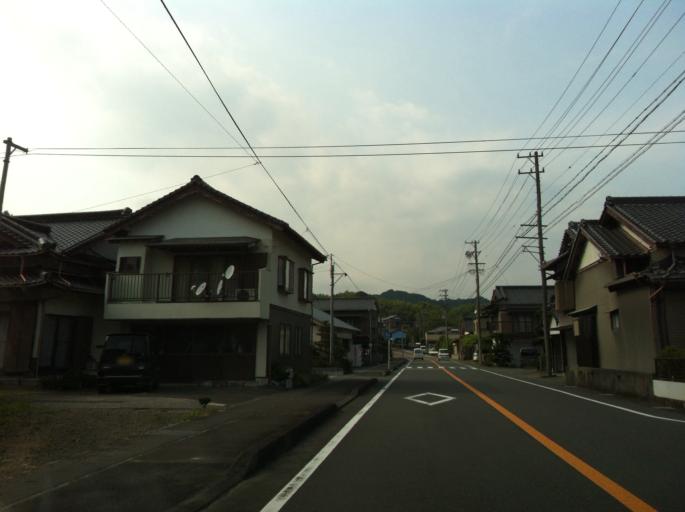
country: JP
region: Shizuoka
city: Fujieda
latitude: 34.9404
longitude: 138.2593
